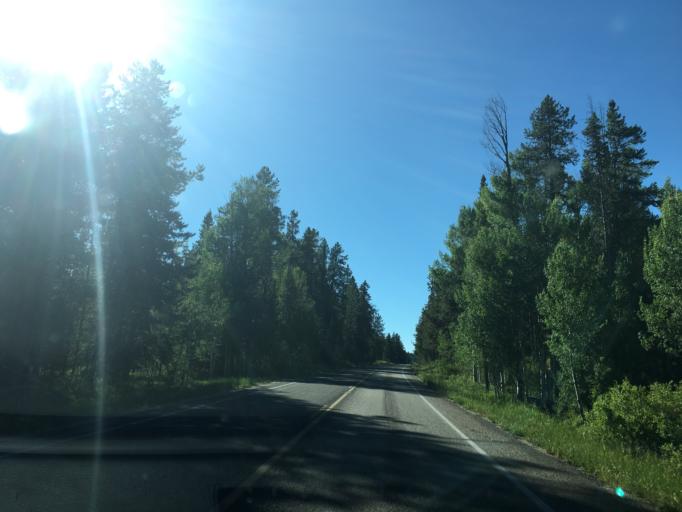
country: US
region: Wyoming
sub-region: Teton County
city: Jackson
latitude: 43.8563
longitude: -110.5247
